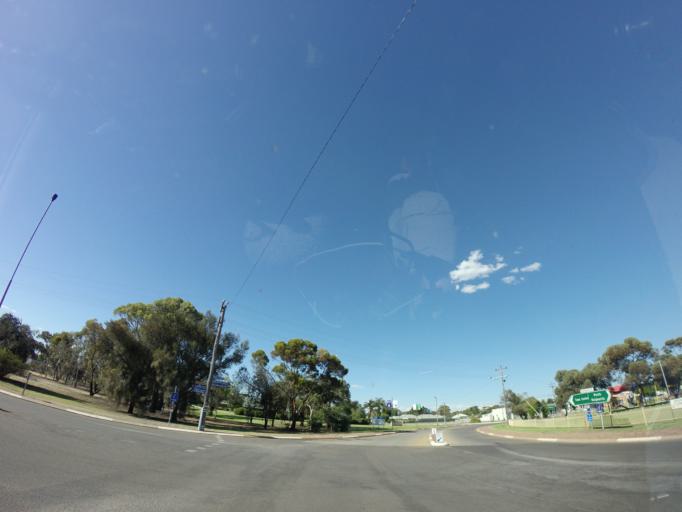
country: AU
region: Western Australia
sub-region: Merredin
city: Merredin
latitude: -31.4821
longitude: 118.2725
